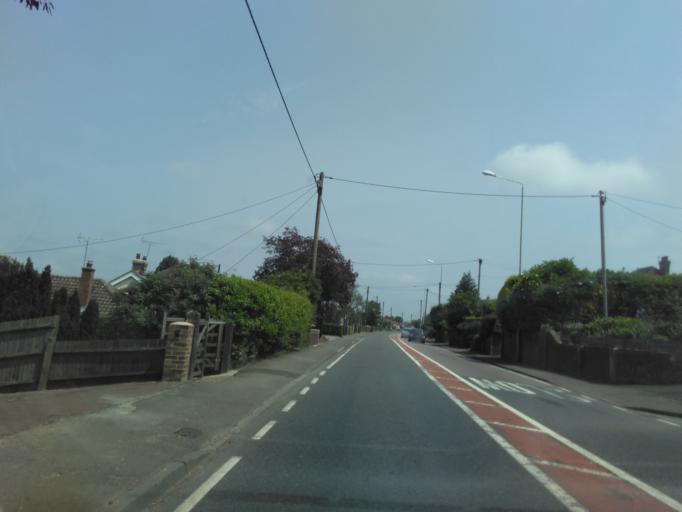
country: GB
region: England
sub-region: Kent
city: Chartham
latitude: 51.2686
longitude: 1.0457
